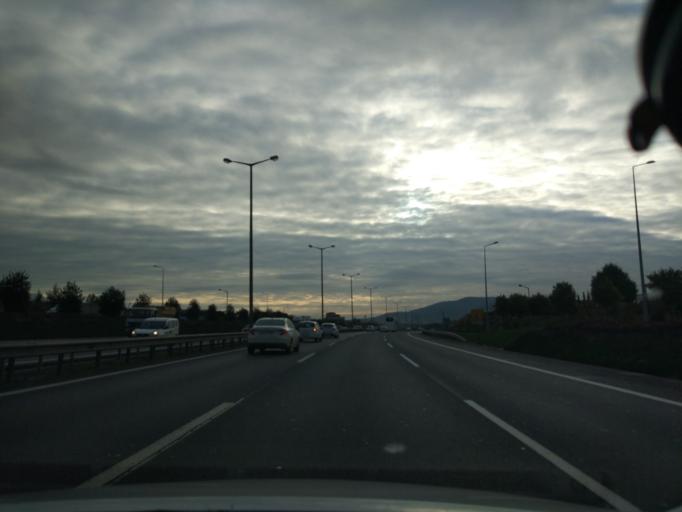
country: TR
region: Istanbul
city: Samandira
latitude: 40.9885
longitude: 29.1933
